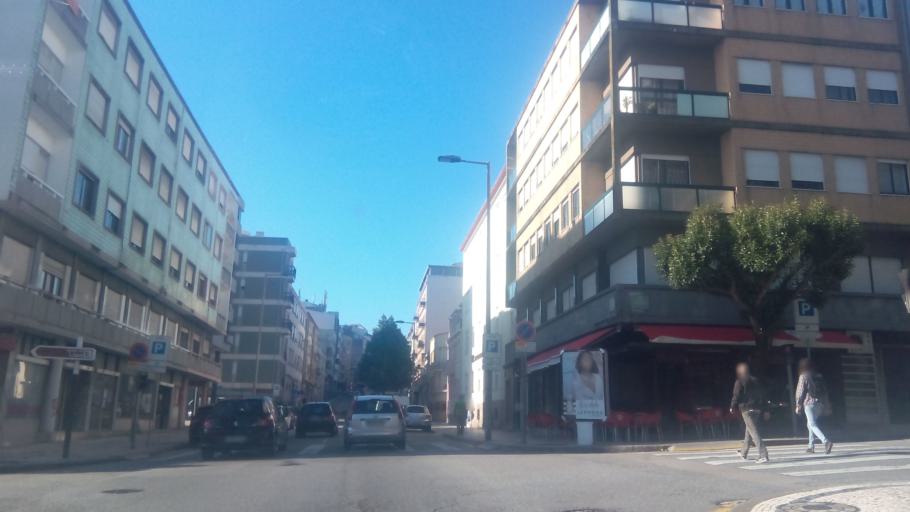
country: PT
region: Porto
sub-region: Porto
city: Porto
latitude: 41.1550
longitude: -8.6092
